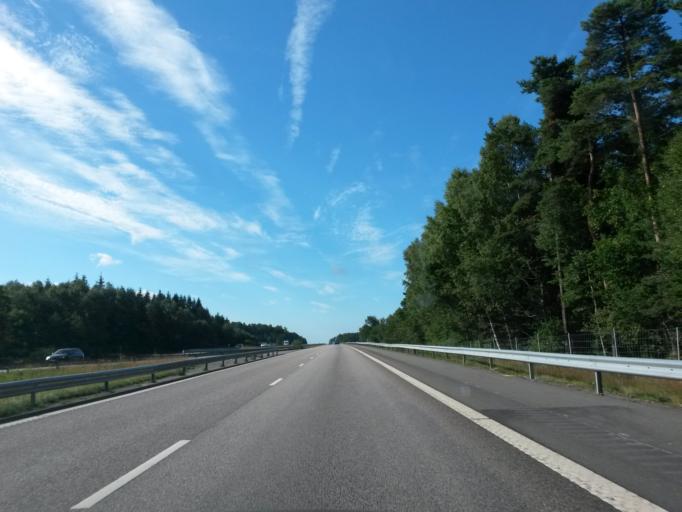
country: SE
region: Halland
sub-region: Kungsbacka Kommun
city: Frillesas
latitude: 57.2819
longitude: 12.2155
